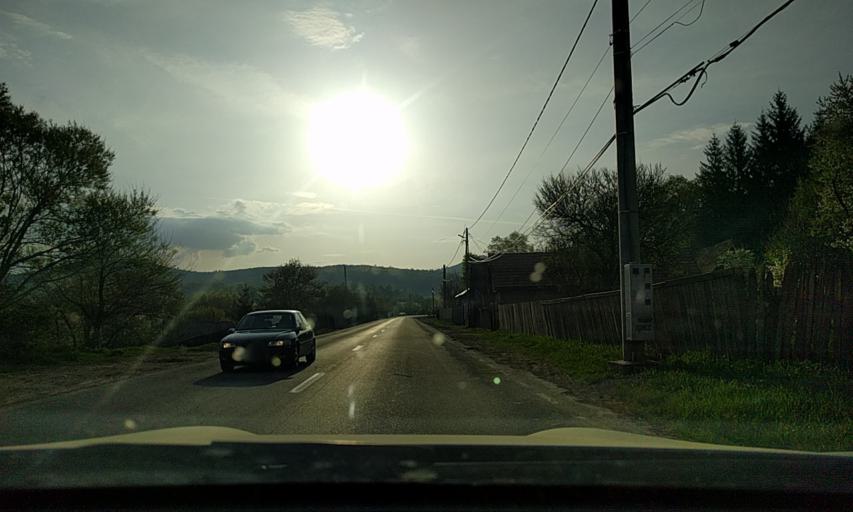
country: RO
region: Covasna
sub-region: Comuna Bretcu
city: Bretcu
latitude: 46.0477
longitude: 26.3161
